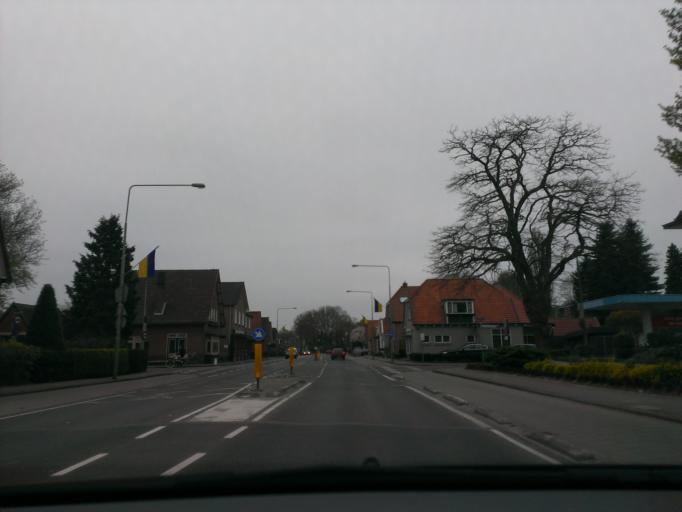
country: NL
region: Gelderland
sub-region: Gemeente Epe
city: Epe
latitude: 52.3437
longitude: 5.9830
